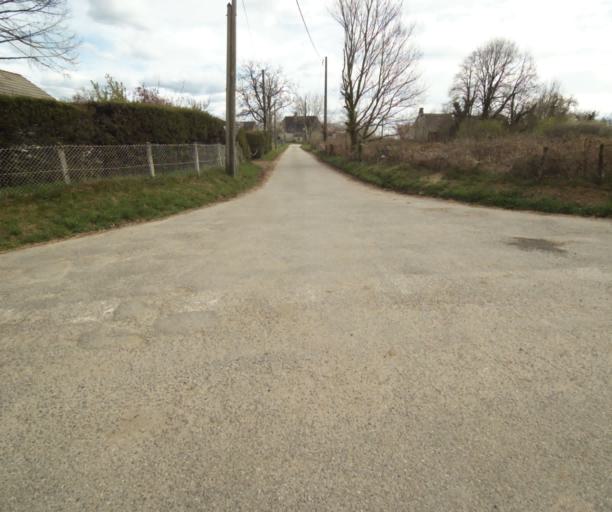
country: FR
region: Limousin
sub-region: Departement de la Correze
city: Argentat
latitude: 45.1824
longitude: 1.9219
